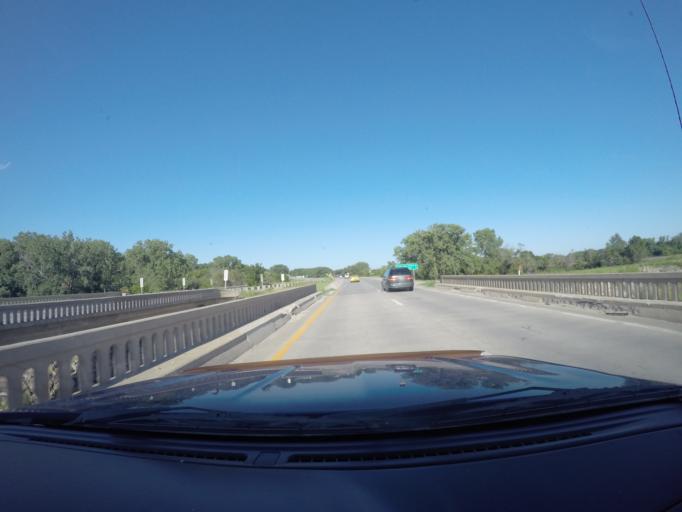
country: US
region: Kansas
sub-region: Shawnee County
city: Topeka
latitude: 39.0911
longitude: -95.6282
